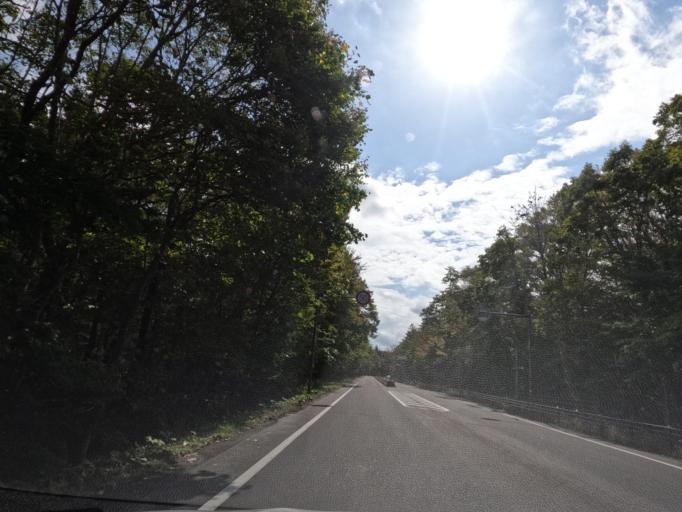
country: JP
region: Hokkaido
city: Chitose
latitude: 42.7996
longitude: 141.5680
